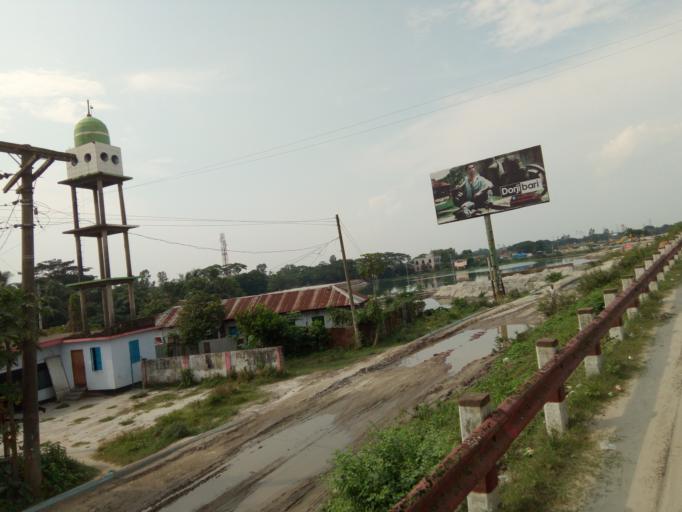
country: BD
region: Dhaka
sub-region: Dhaka
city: Dhaka
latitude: 23.6329
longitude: 90.3449
